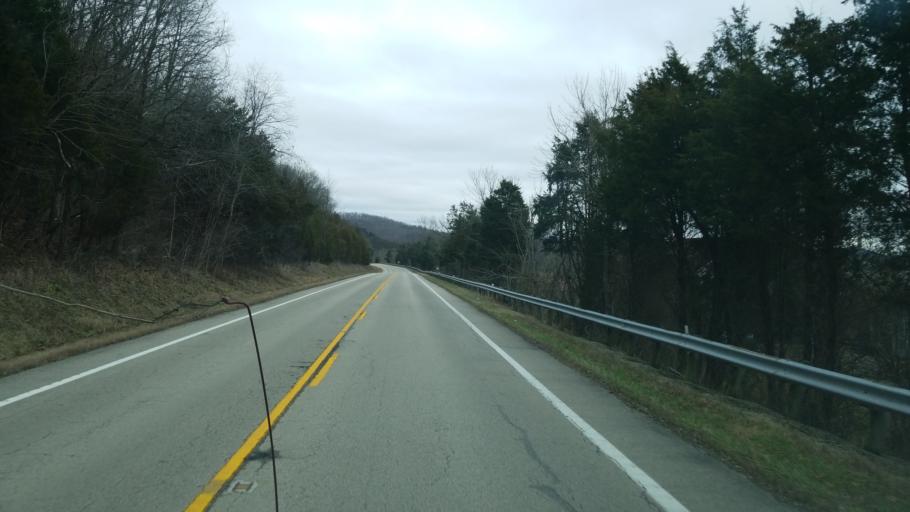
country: US
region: Ohio
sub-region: Adams County
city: Manchester
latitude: 38.7054
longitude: -83.5304
